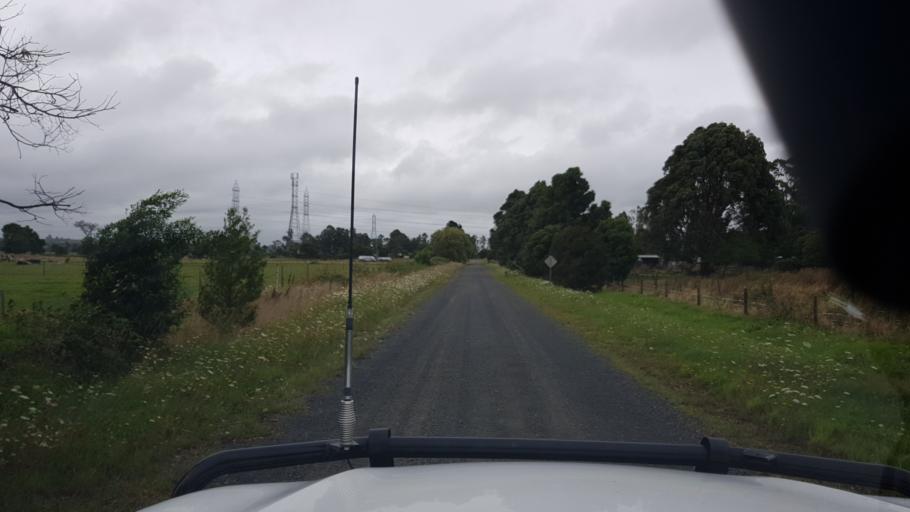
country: AU
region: Victoria
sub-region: Cardinia
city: Bunyip
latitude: -38.0816
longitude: 145.7838
